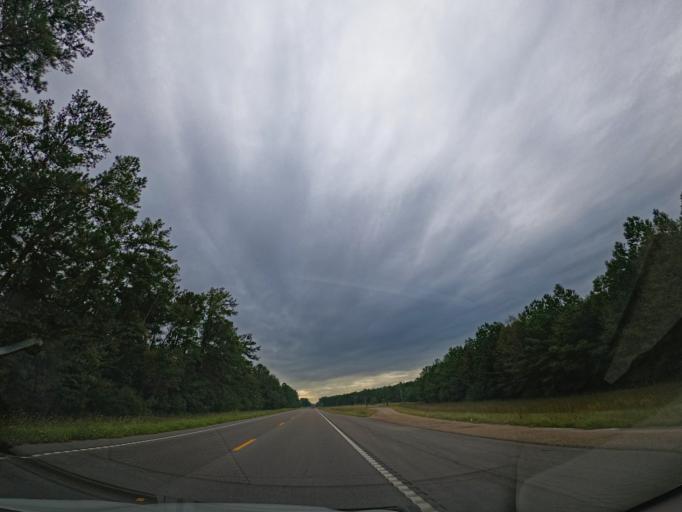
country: US
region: Mississippi
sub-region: Hancock County
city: Pearlington
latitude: 30.2716
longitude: -89.5537
